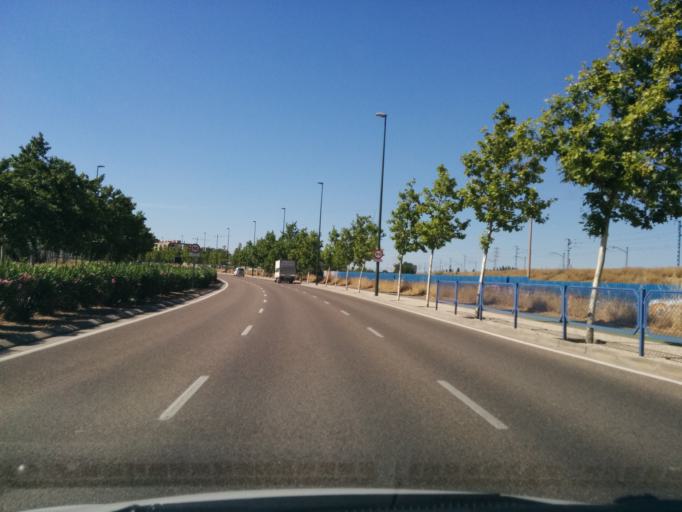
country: ES
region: Aragon
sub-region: Provincia de Zaragoza
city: Zaragoza
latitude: 41.6573
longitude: -0.8530
